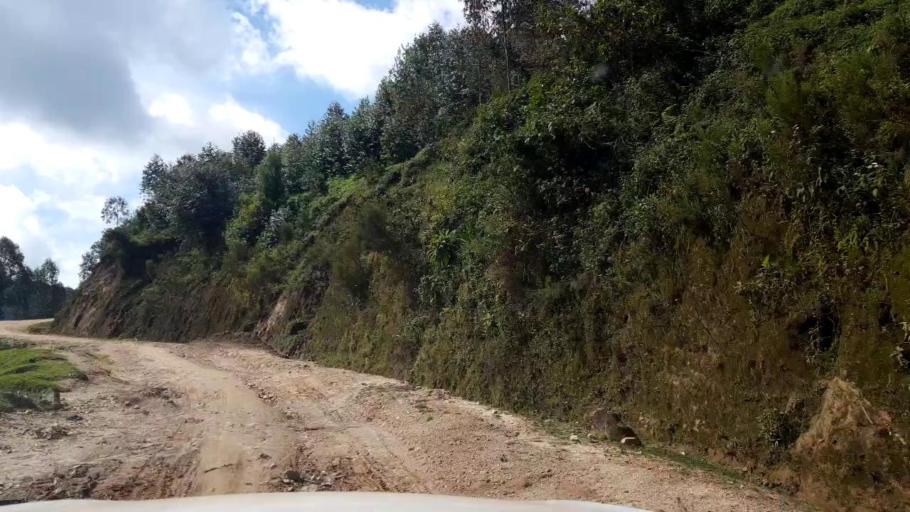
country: RW
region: Western Province
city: Kibuye
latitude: -1.8845
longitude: 29.4687
